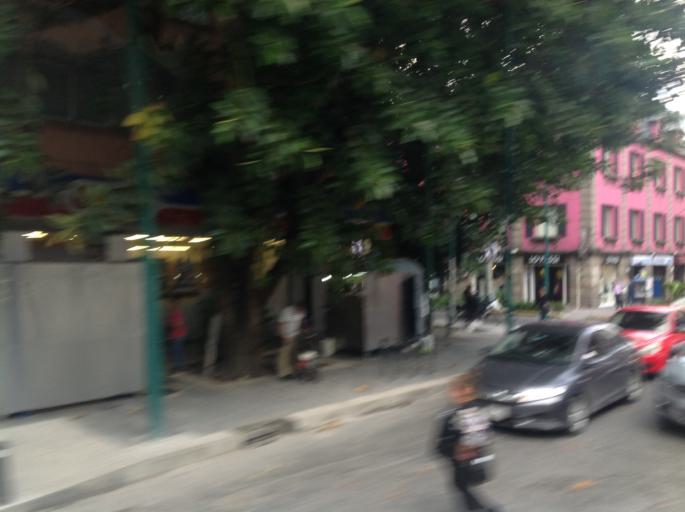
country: MX
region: Mexico City
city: Cuauhtemoc
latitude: 19.4265
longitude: -99.1613
